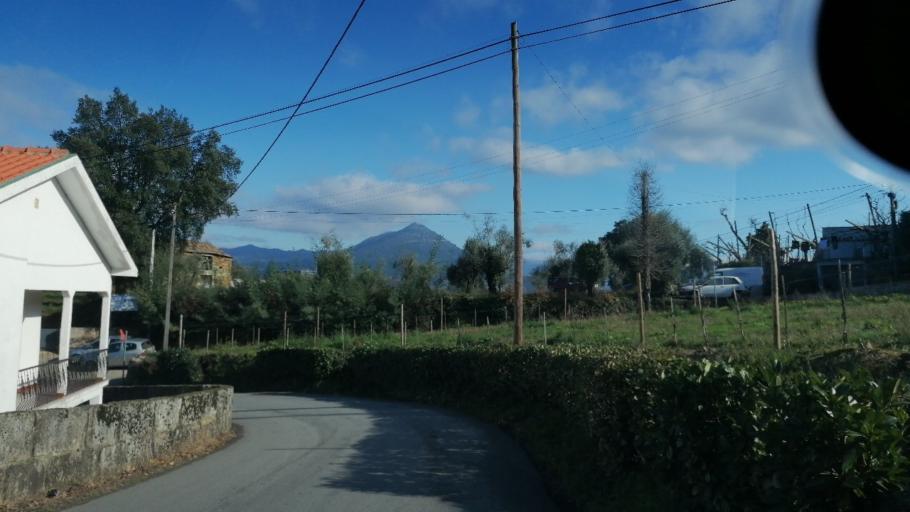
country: PT
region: Braga
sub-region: Celorico de Basto
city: Celorico de Basto
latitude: 41.4082
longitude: -7.9880
